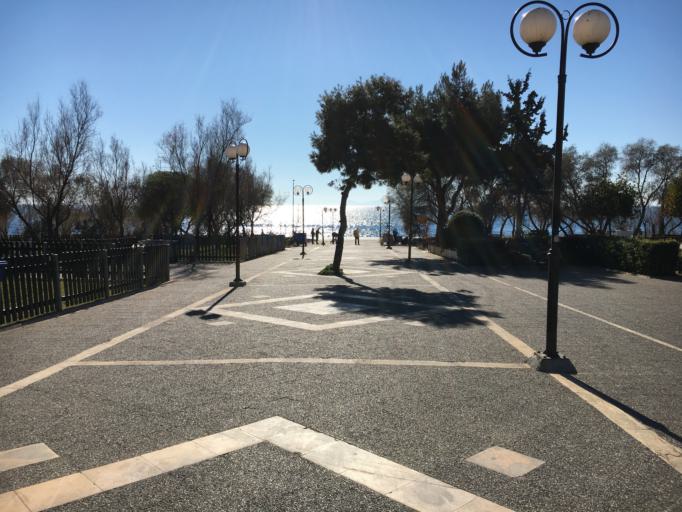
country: GR
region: Attica
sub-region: Nomarchia Athinas
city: Palaio Faliro
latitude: 37.9277
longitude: 23.6875
